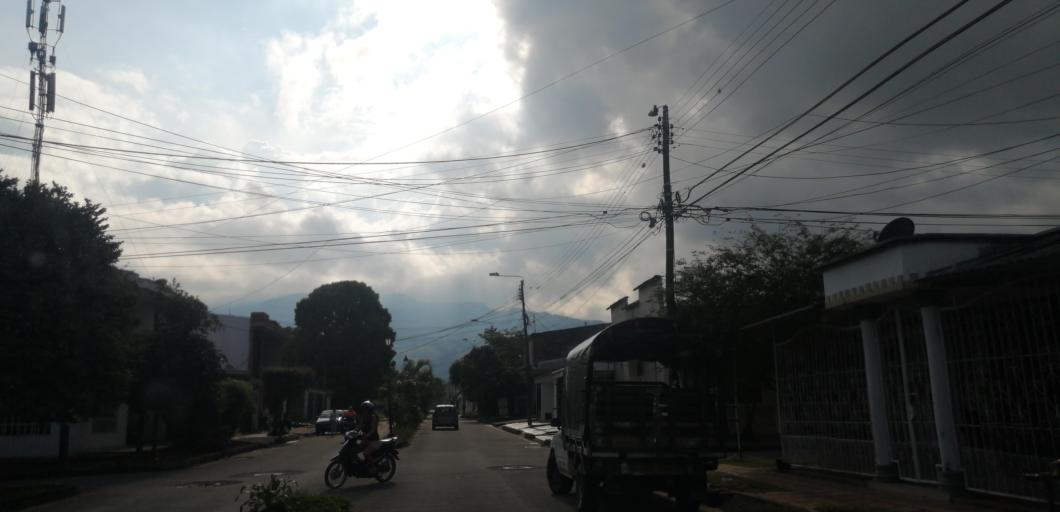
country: CO
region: Meta
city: Acacias
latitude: 3.9862
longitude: -73.7742
